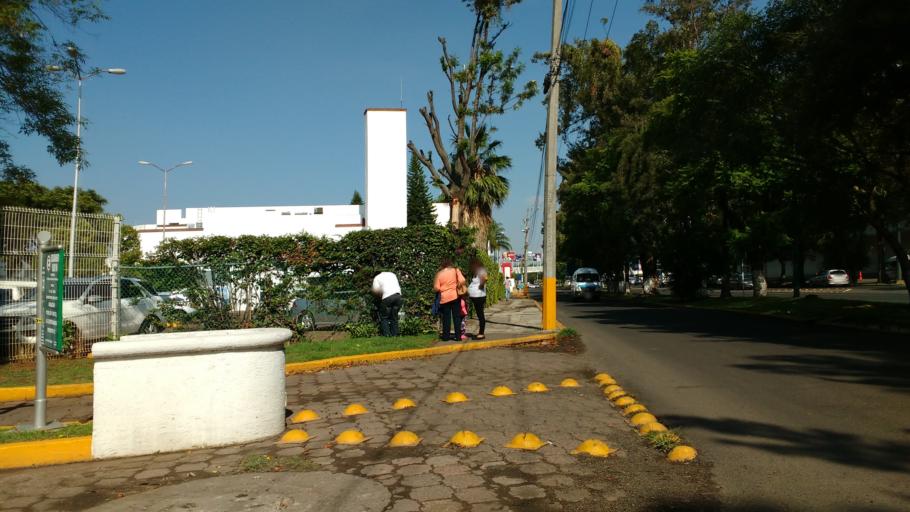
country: MX
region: Michoacan
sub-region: Morelia
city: Montana Monarca (Punta Altozano)
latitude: 19.6874
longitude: -101.1560
